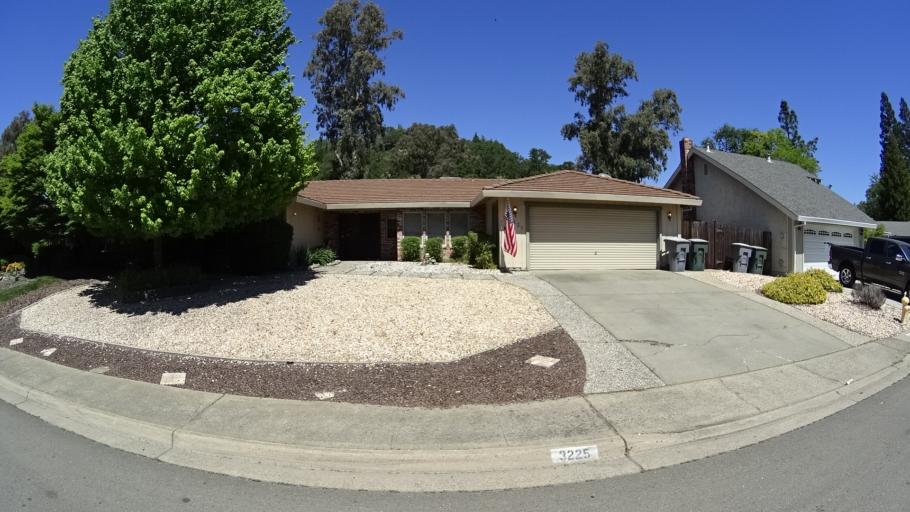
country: US
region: California
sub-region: Placer County
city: Rocklin
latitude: 38.7983
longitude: -121.2432
